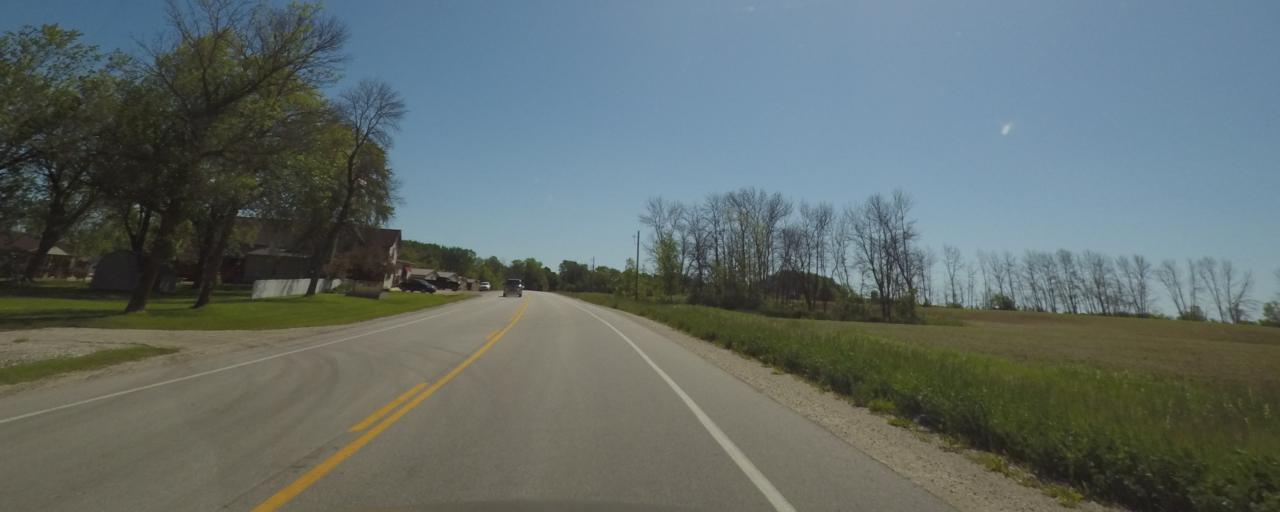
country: US
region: Wisconsin
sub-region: Sheboygan County
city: Plymouth
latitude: 43.7460
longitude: -87.9176
